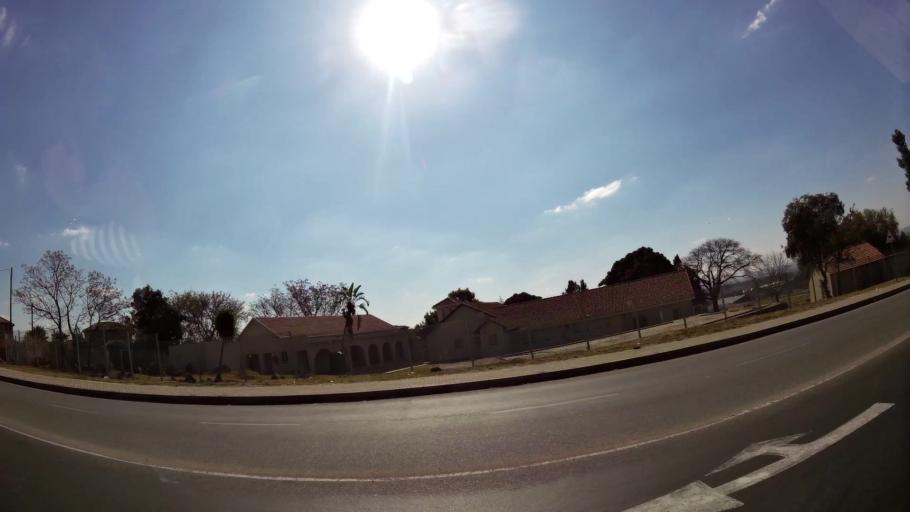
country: ZA
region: Gauteng
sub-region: West Rand District Municipality
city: Muldersdriseloop
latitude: -26.0226
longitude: 27.9406
